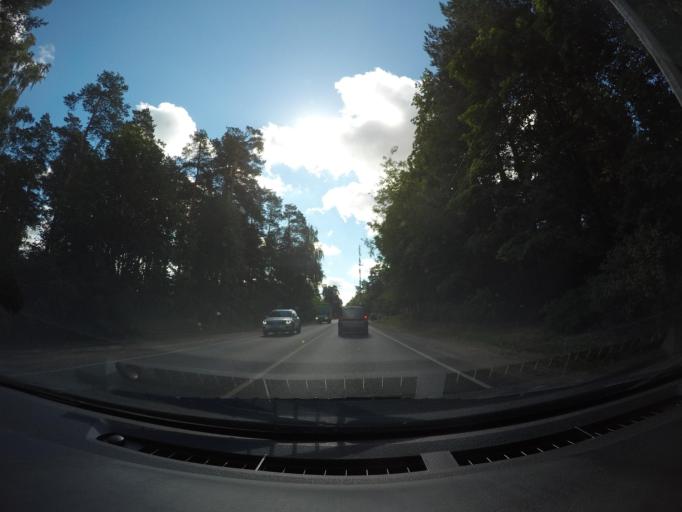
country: RU
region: Moskovskaya
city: Kratovo
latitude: 55.5906
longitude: 38.1882
